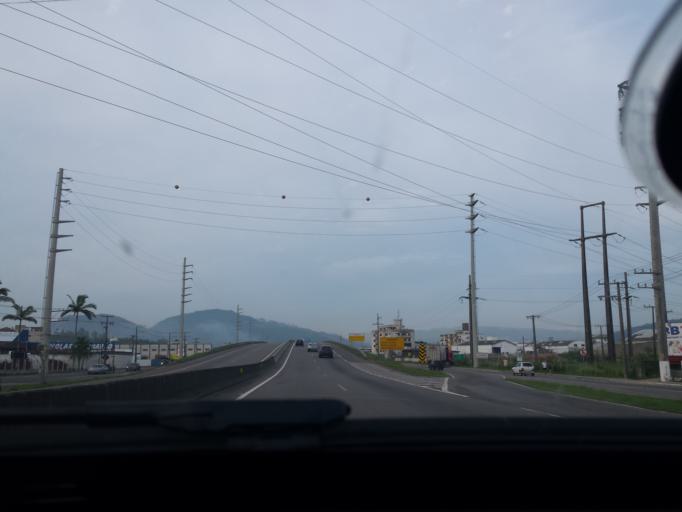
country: BR
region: Santa Catarina
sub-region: Tubarao
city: Tubarao
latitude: -28.4687
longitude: -49.0126
